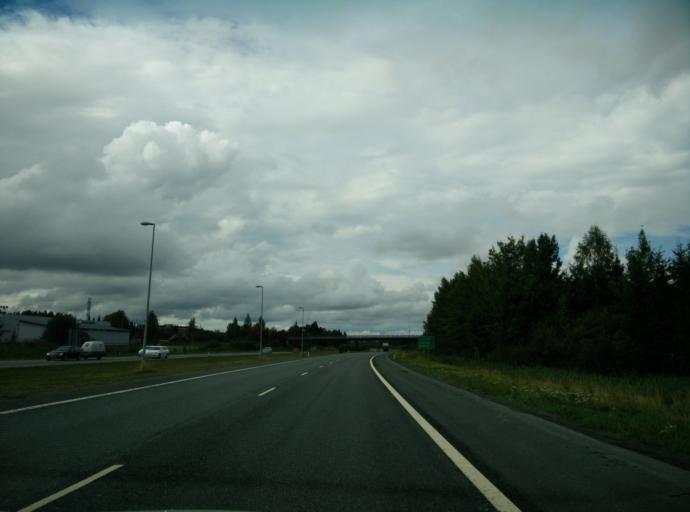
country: FI
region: Haeme
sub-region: Haemeenlinna
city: Haemeenlinna
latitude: 61.0173
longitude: 24.4098
